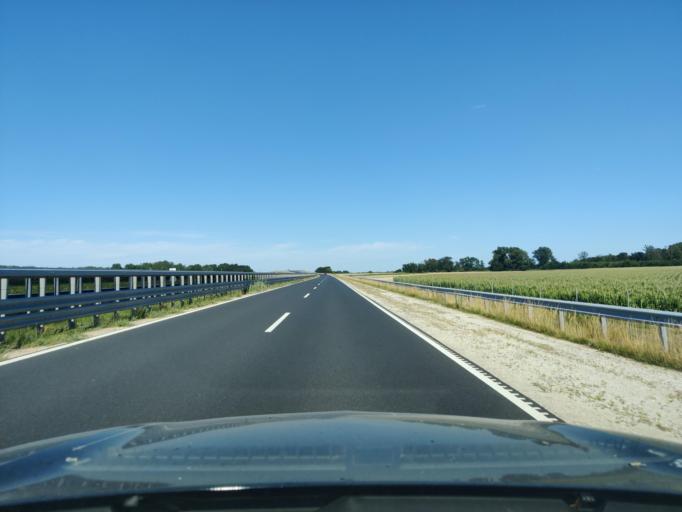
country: HU
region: Vas
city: Repcelak
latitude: 47.4173
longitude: 17.0470
